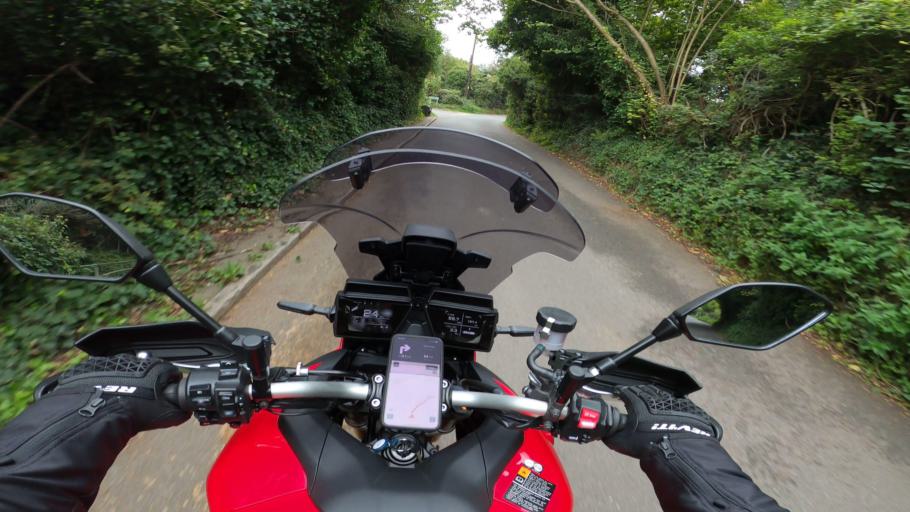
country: GB
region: England
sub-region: Kent
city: Halstead
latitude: 51.3539
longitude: 0.1371
